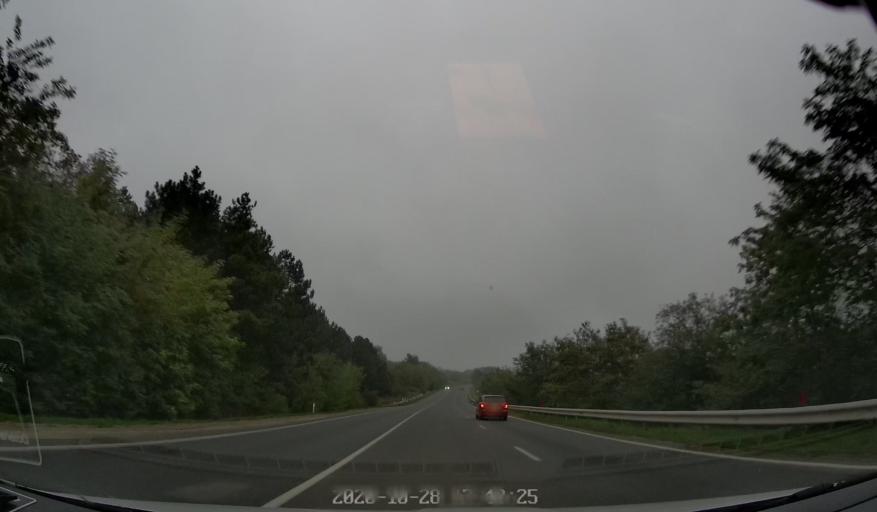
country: MD
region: Hincesti
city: Hincesti
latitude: 46.8756
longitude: 28.6491
